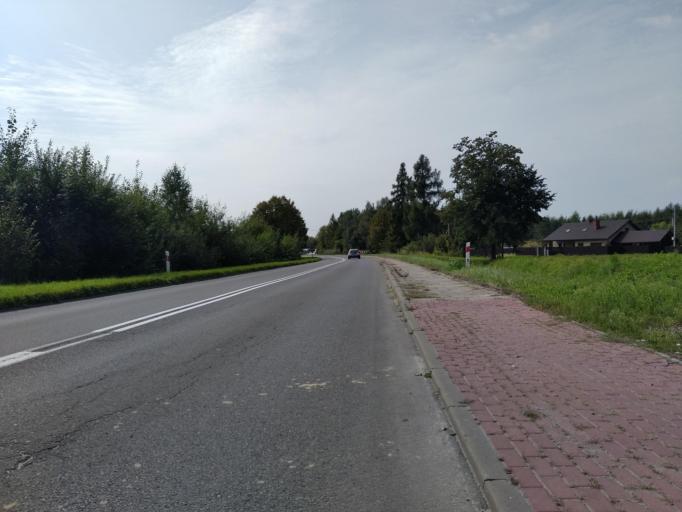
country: PL
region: Subcarpathian Voivodeship
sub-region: Powiat ropczycko-sedziszowski
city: Ostrow
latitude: 50.0839
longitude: 21.5853
